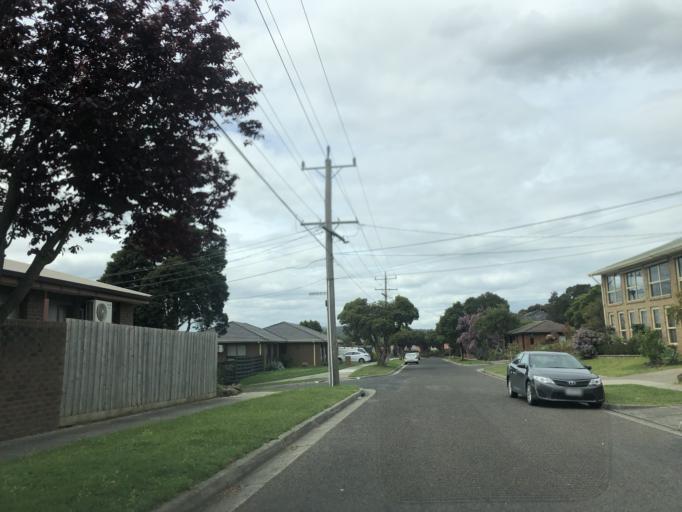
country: AU
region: Victoria
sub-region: Knox
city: Rowville
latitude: -37.9415
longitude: 145.2138
